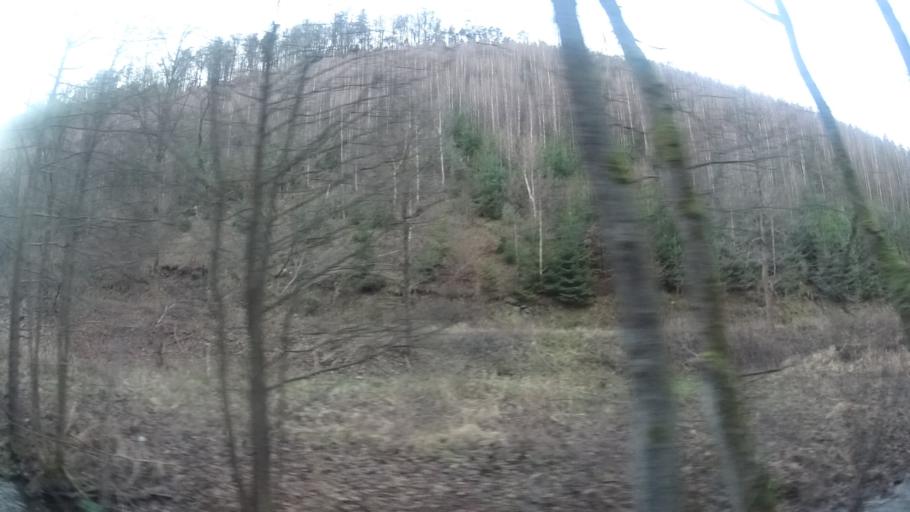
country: DE
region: Thuringia
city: Rohrbach
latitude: 50.6193
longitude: 11.2107
